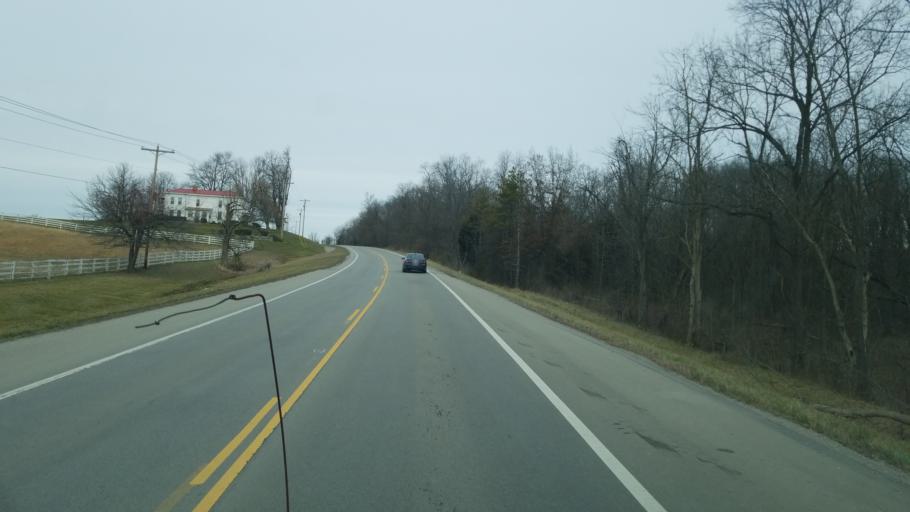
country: US
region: Ohio
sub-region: Adams County
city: Winchester
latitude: 39.0026
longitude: -83.7101
